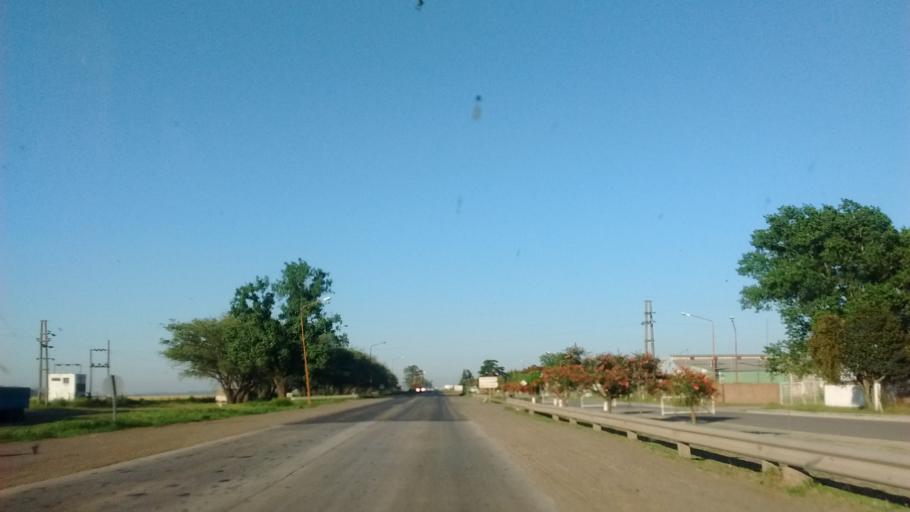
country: AR
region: Santa Fe
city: Venado Tuerto
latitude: -33.6468
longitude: -61.8581
